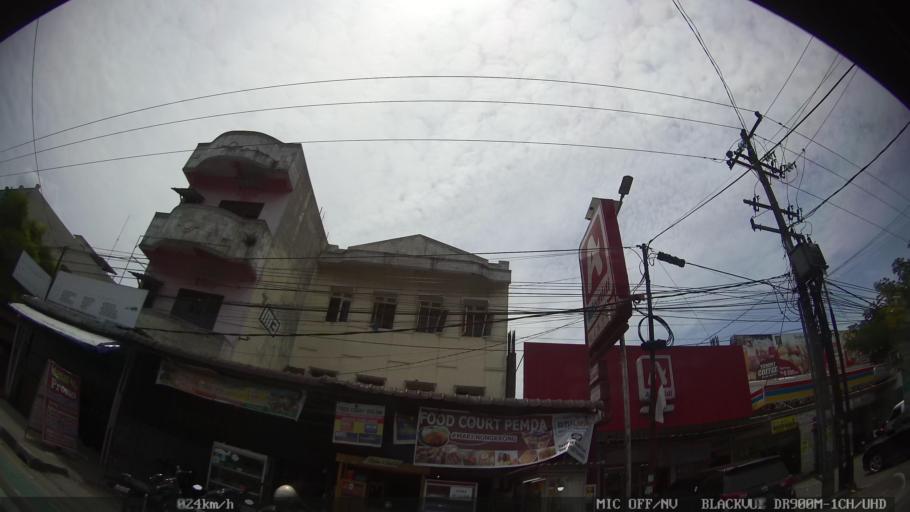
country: ID
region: North Sumatra
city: Sunggal
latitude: 3.5432
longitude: 98.6241
